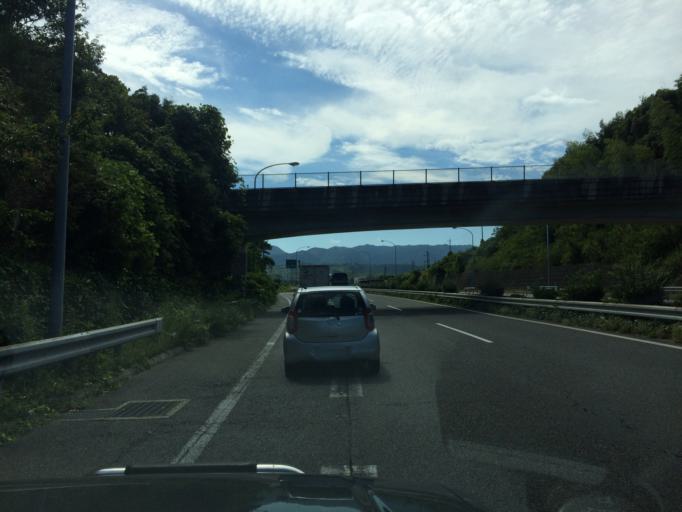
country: JP
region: Osaka
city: Izumi
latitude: 34.4416
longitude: 135.4435
